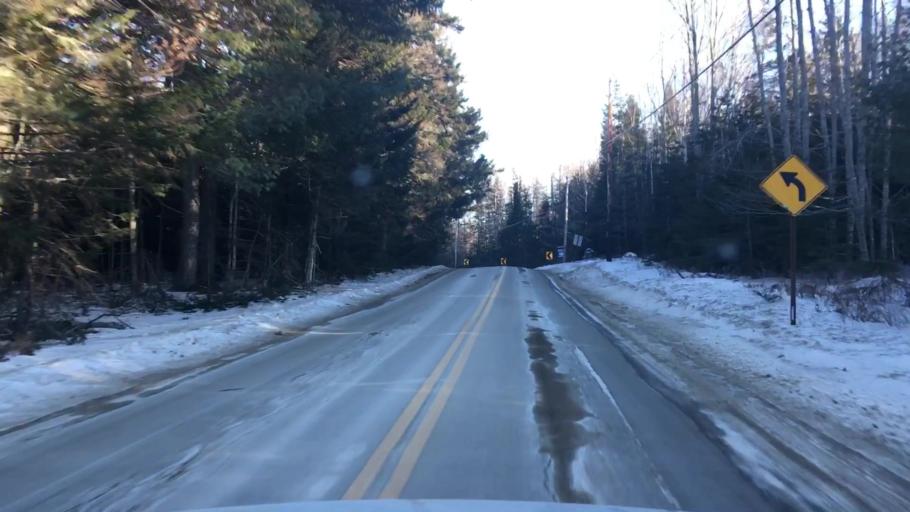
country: US
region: Maine
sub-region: Hancock County
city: Penobscot
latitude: 44.3976
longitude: -68.7023
